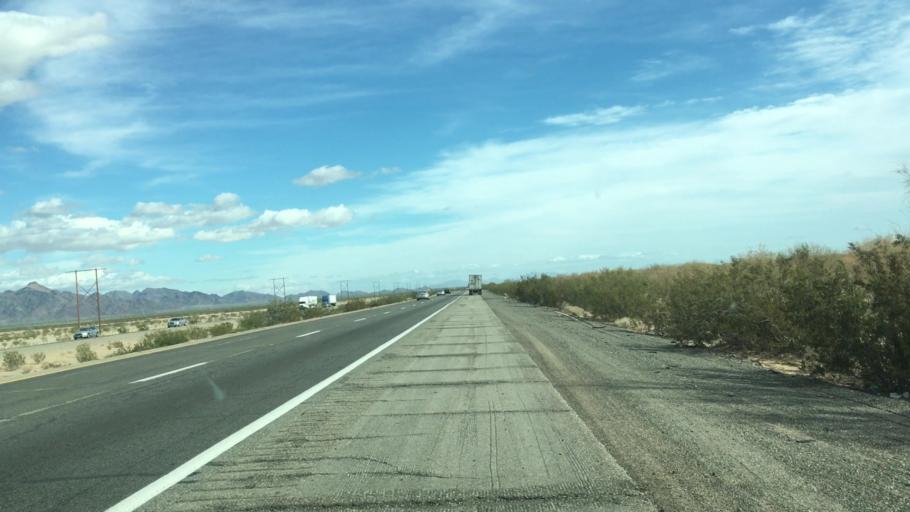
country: US
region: California
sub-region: Riverside County
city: Mesa Verde
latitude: 33.6058
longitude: -114.9636
